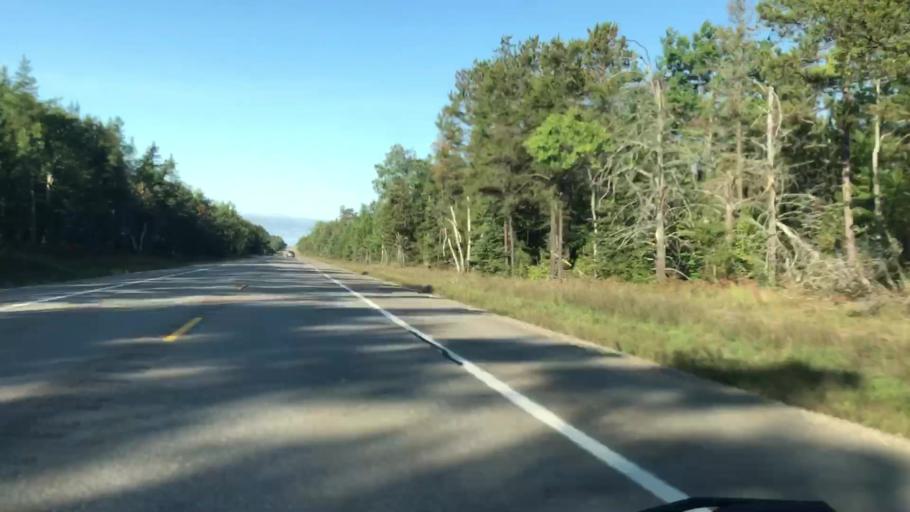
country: US
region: Michigan
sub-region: Chippewa County
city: Sault Ste. Marie
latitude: 46.3687
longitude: -84.7426
